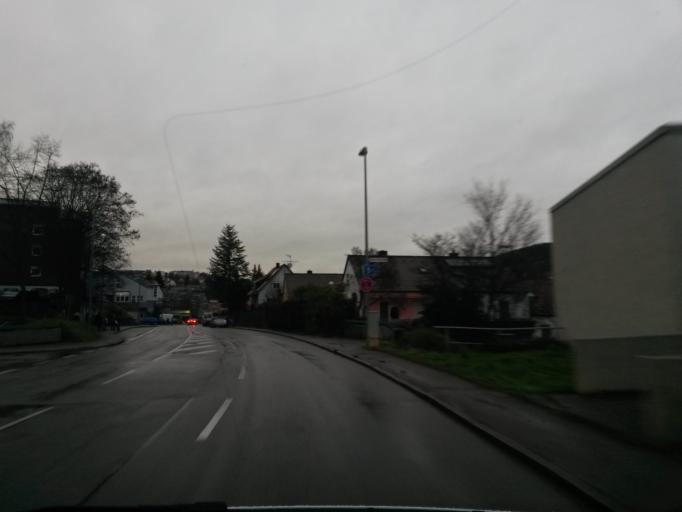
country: DE
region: Baden-Wuerttemberg
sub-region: Regierungsbezirk Stuttgart
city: Esslingen
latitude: 48.7465
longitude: 9.3242
